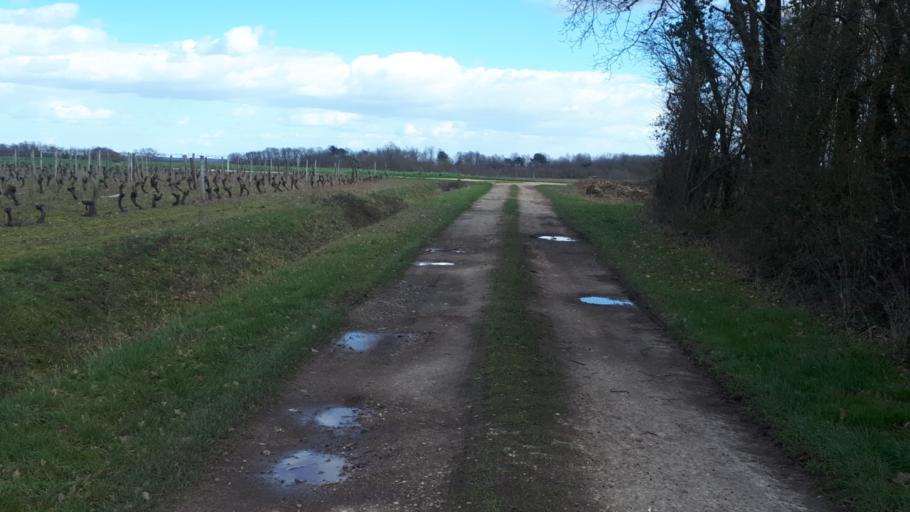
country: FR
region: Centre
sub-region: Departement du Loir-et-Cher
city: Villiers-sur-Loir
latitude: 47.8054
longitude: 1.0099
